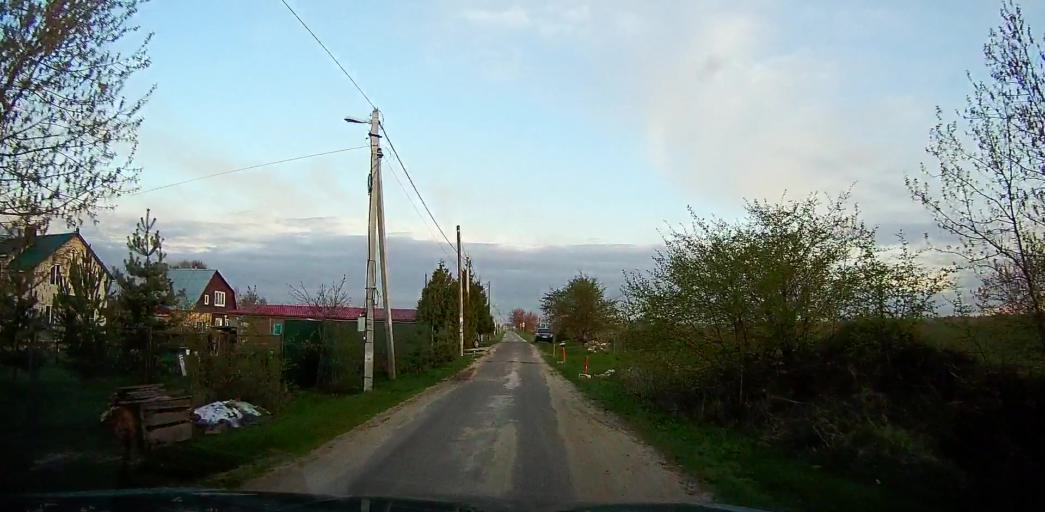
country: RU
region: Moskovskaya
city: Peski
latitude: 55.2312
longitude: 38.7328
